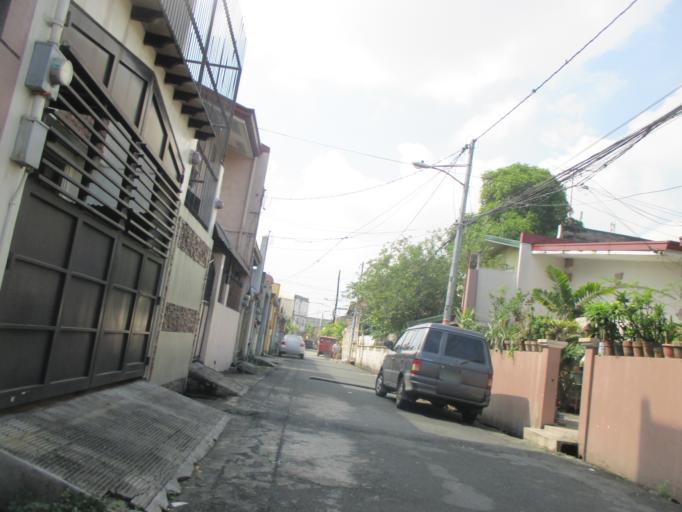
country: PH
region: Metro Manila
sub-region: Marikina
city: Calumpang
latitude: 14.6213
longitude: 121.0894
